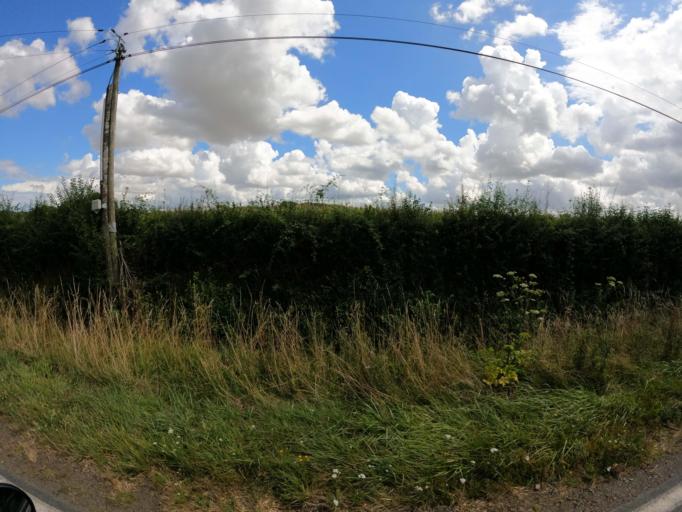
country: FR
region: Pays de la Loire
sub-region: Departement de la Sarthe
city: Juigne-sur-Sarthe
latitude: 47.8907
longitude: -0.2911
